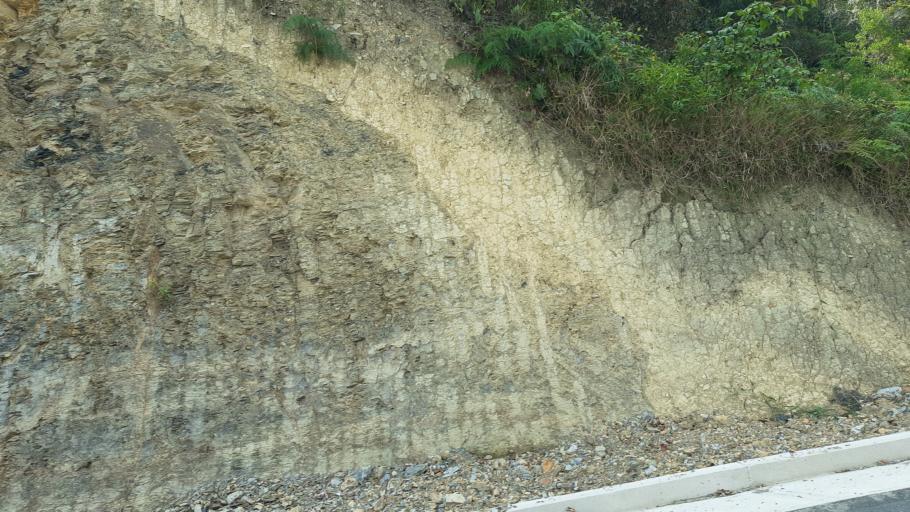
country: CO
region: Boyaca
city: Santa Sofia
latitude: 5.7800
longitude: -73.6047
